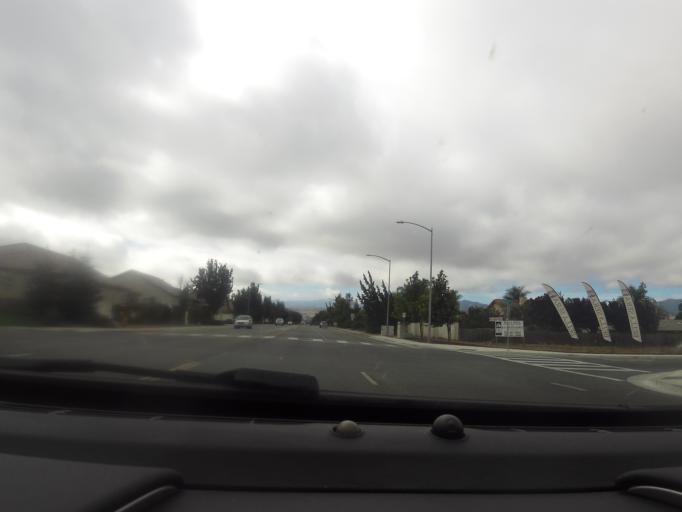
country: US
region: California
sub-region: San Benito County
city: Hollister
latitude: 36.8372
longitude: -121.3929
